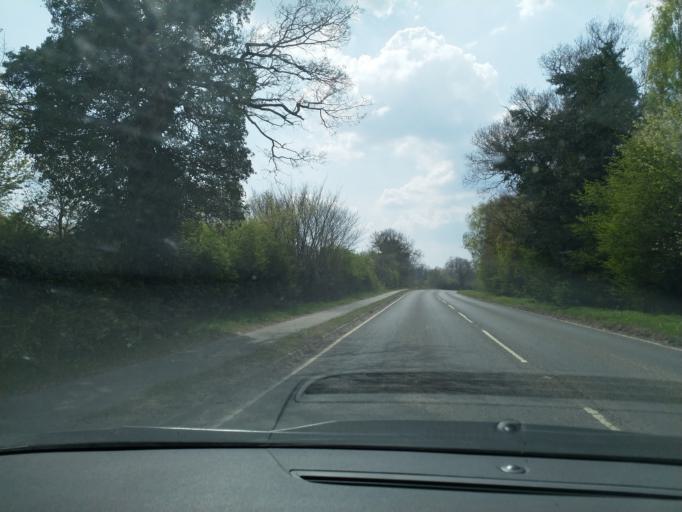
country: GB
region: England
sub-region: Warwickshire
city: Ryton on Dunsmore
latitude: 52.3556
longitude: -1.4432
